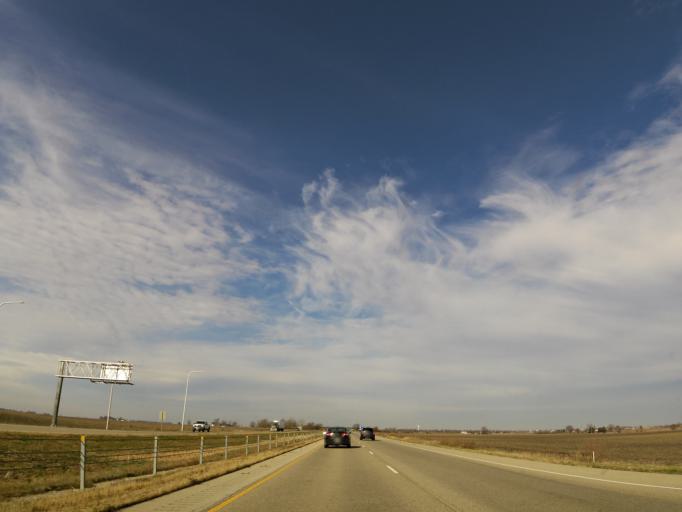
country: US
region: Illinois
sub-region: McLean County
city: Twin Grove
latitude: 40.5601
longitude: -89.1101
